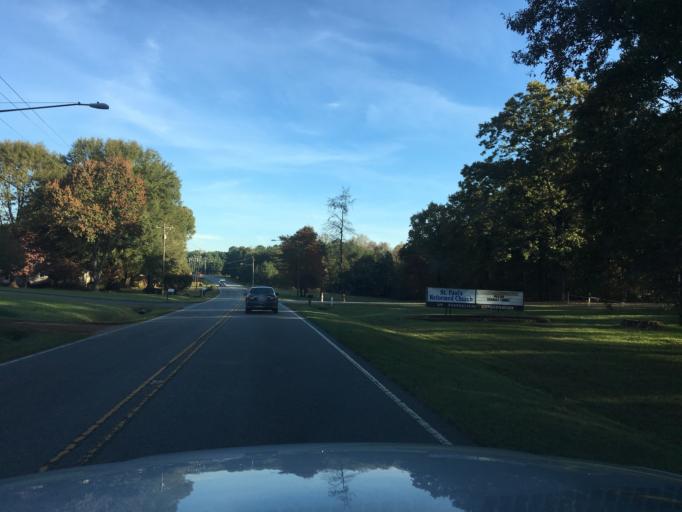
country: US
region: North Carolina
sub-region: Catawba County
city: Newton
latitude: 35.6535
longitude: -81.2664
